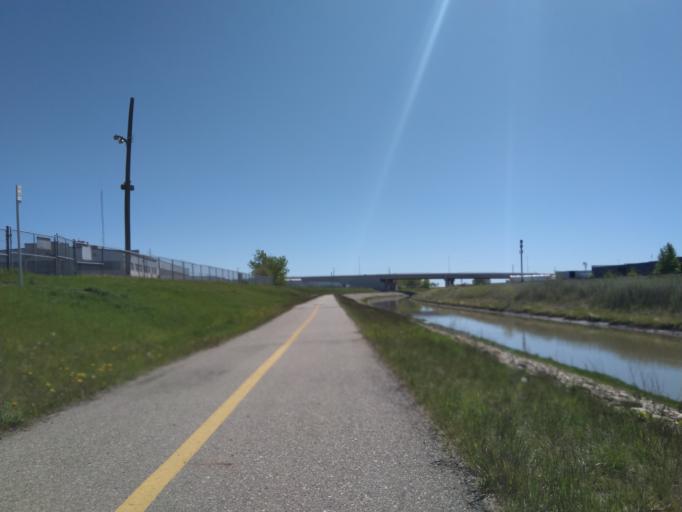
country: CA
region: Alberta
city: Calgary
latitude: 50.9645
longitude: -113.9646
